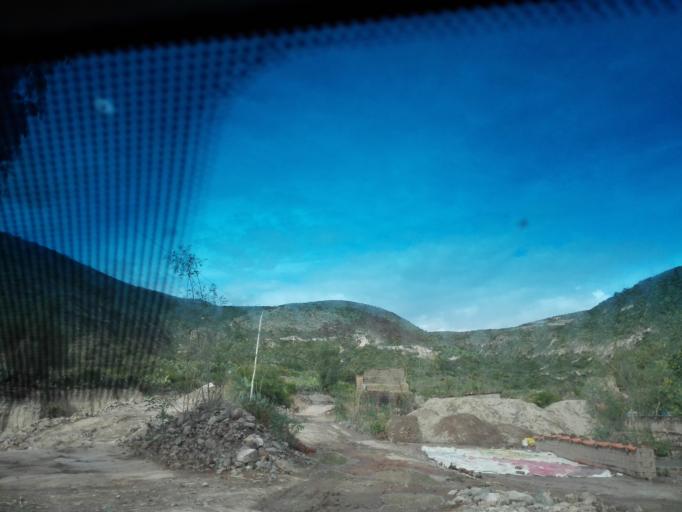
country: PE
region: Ayacucho
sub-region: Provincia de Huamanga
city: Pacaycasa
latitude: -13.0663
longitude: -74.2478
